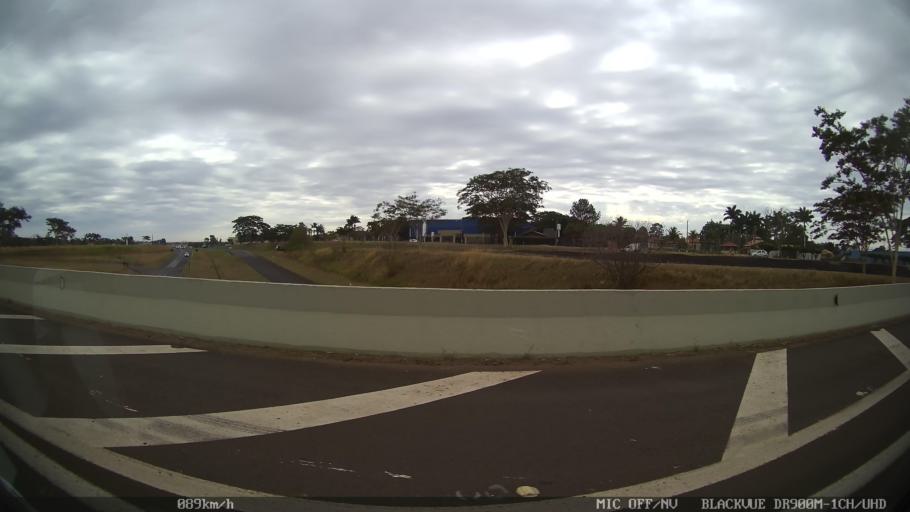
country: BR
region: Sao Paulo
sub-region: Bady Bassitt
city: Bady Bassitt
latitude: -20.8044
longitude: -49.5244
